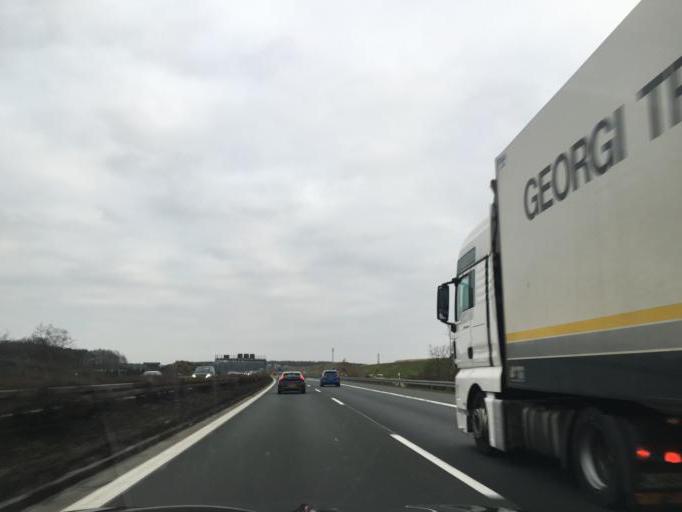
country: DE
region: Bavaria
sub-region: Regierungsbezirk Mittelfranken
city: Hessdorf
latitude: 49.5902
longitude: 10.9262
